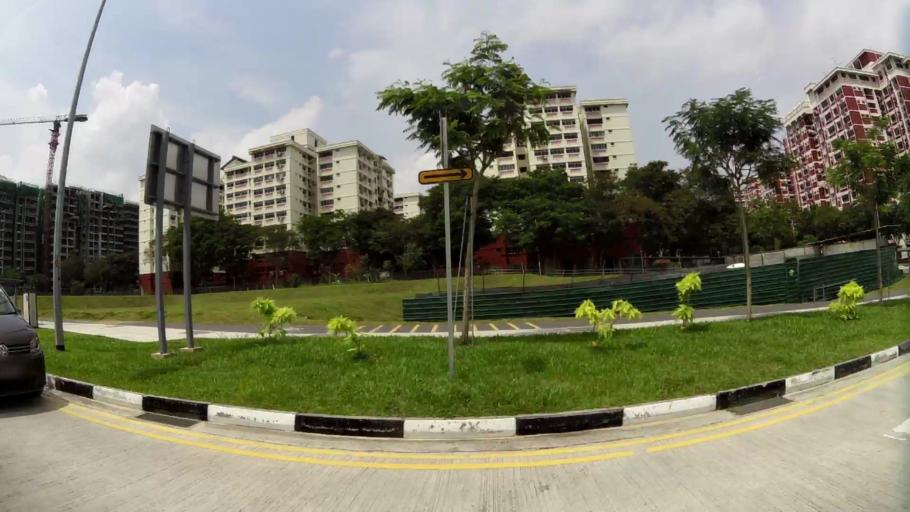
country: MY
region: Johor
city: Kampung Pasir Gudang Baru
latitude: 1.3732
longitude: 103.9479
